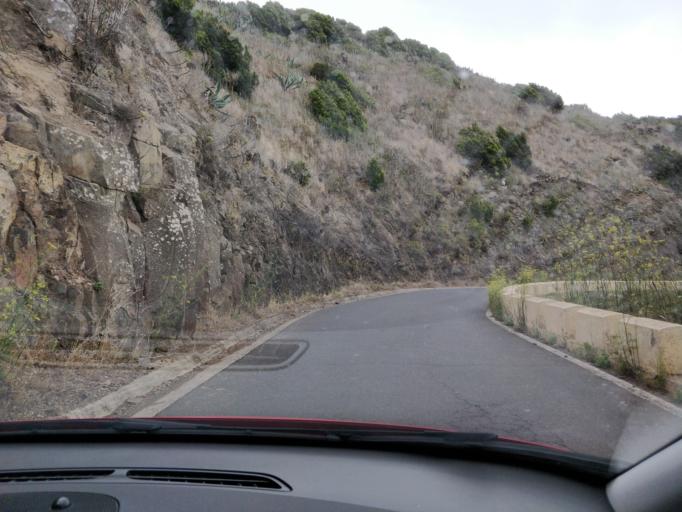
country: ES
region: Canary Islands
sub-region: Provincia de Santa Cruz de Tenerife
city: Tanque
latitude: 28.3268
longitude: -16.8551
